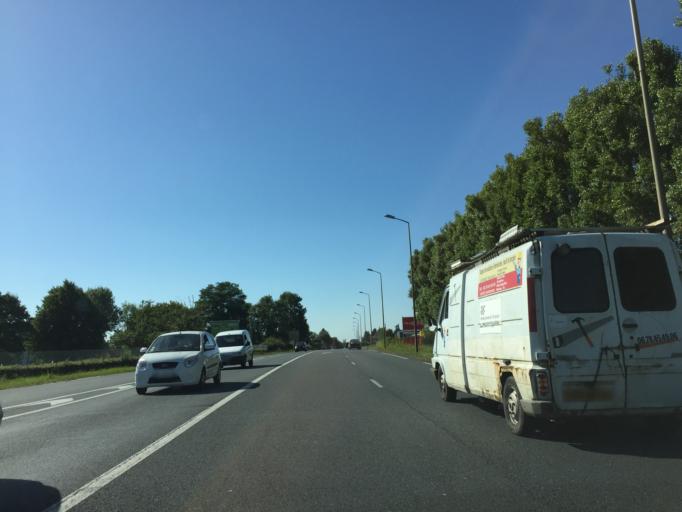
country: FR
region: Lower Normandy
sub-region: Departement du Calvados
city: Beuvillers
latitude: 49.1459
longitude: 0.2608
